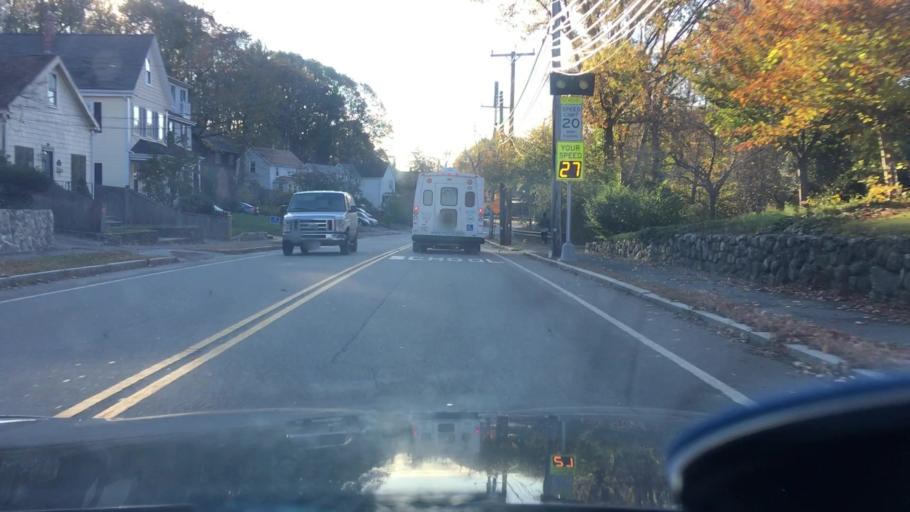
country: US
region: Massachusetts
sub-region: Norfolk County
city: Needham
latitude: 42.3224
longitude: -71.2523
